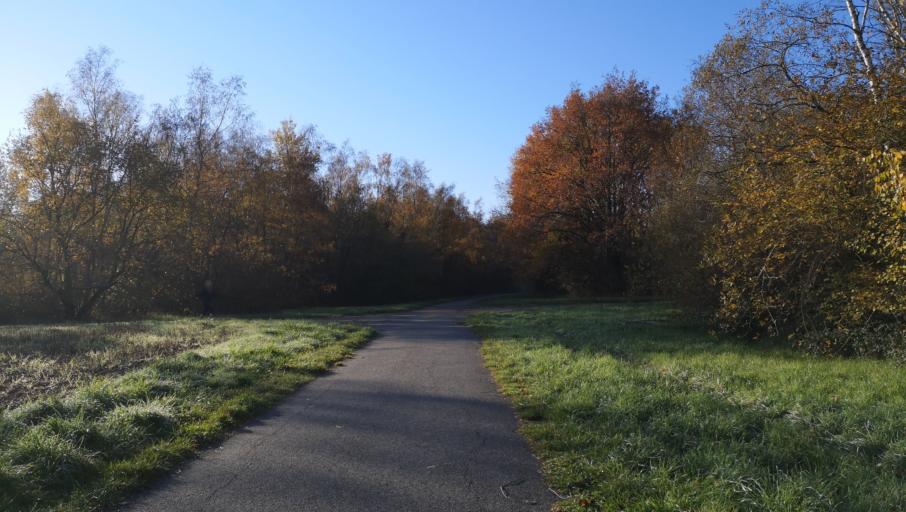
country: FR
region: Centre
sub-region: Departement du Loiret
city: Saran
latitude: 47.9379
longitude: 1.8606
